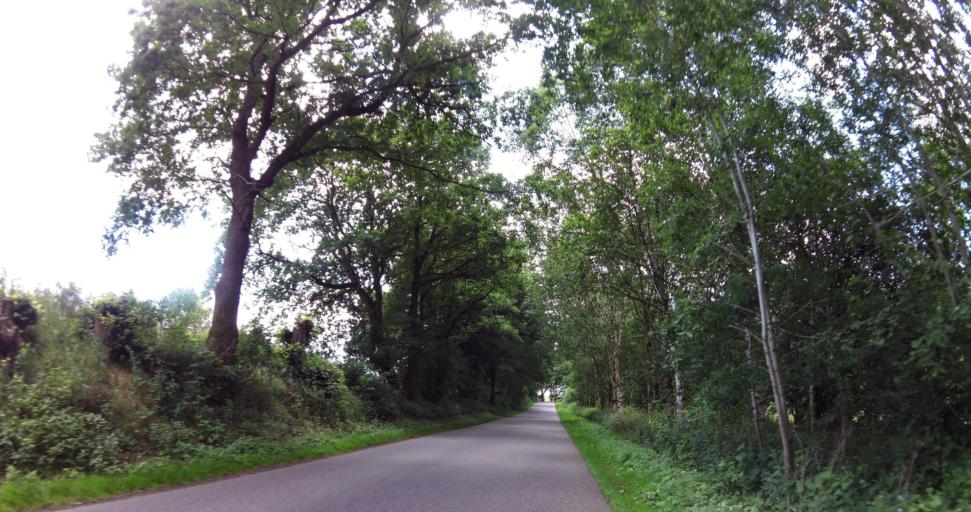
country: DE
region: Schleswig-Holstein
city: Fleckeby
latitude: 54.4967
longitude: 9.7296
